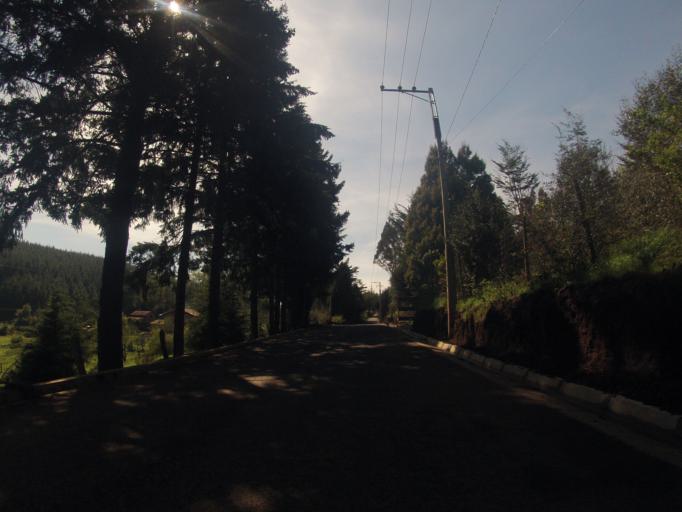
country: CL
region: Araucania
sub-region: Provincia de Cautin
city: Temuco
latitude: -38.6856
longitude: -72.5794
